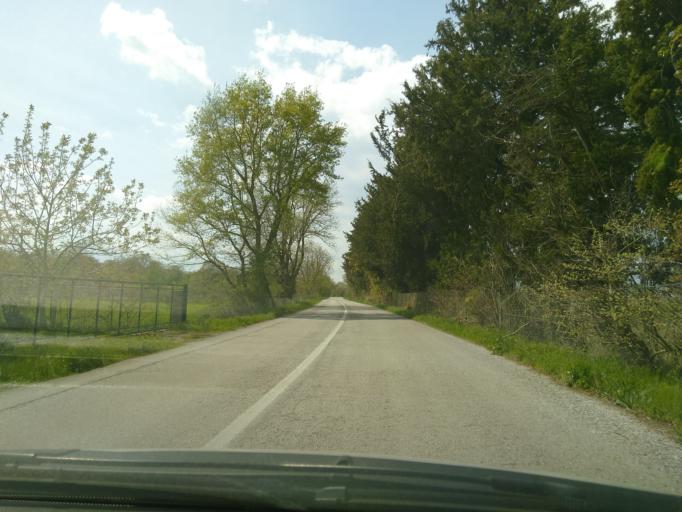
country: GR
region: Epirus
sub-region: Nomos Ioanninon
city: Eleousa
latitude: 39.7370
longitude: 20.7725
